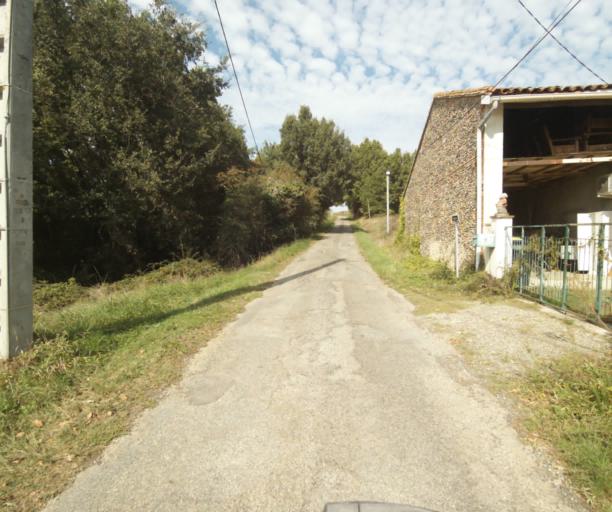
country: FR
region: Midi-Pyrenees
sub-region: Departement du Tarn-et-Garonne
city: Verdun-sur-Garonne
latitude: 43.8564
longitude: 1.1792
